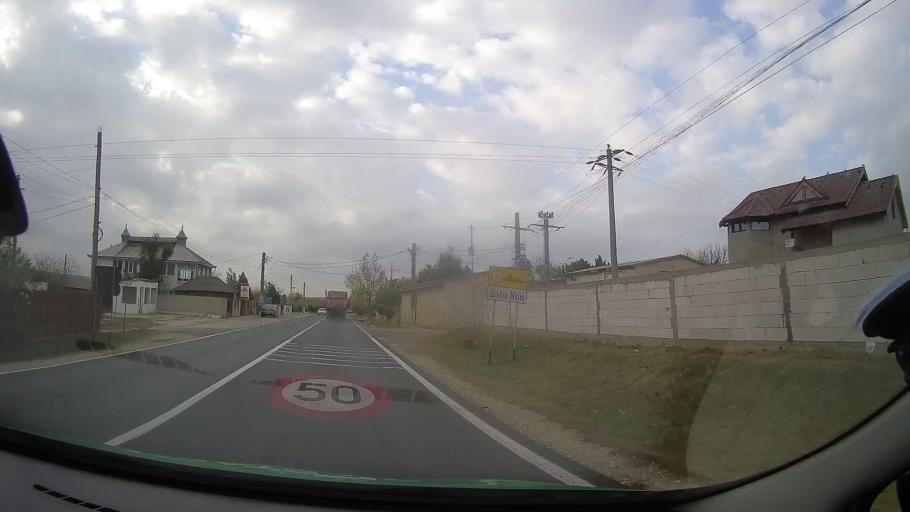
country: RO
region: Constanta
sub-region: Comuna Mircea Voda
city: Satu Nou
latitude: 44.2658
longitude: 28.2325
